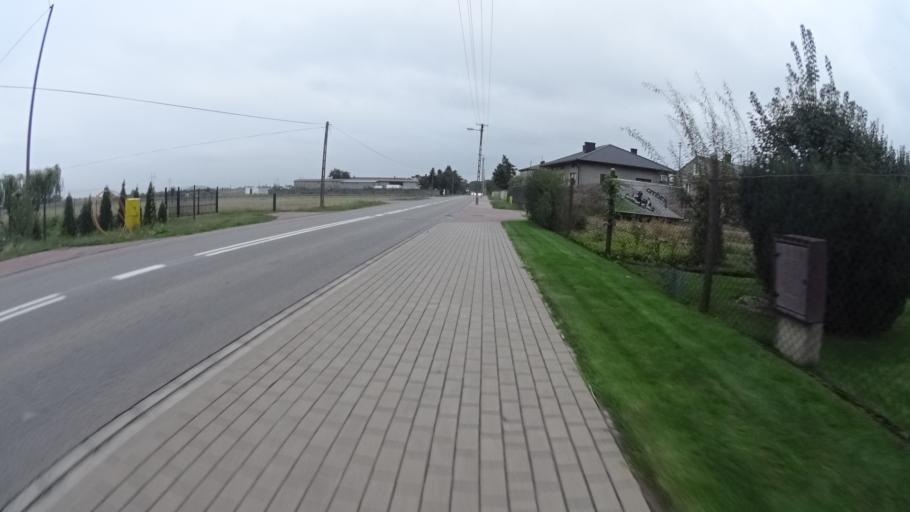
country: PL
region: Masovian Voivodeship
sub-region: Powiat warszawski zachodni
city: Babice
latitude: 52.2296
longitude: 20.8389
